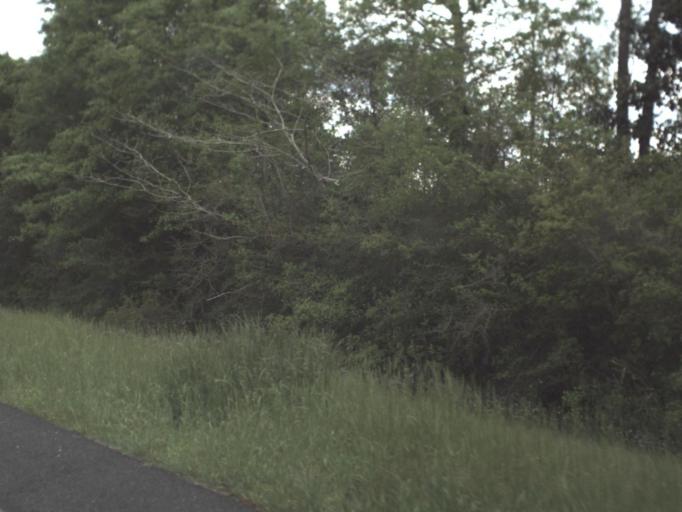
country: US
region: Florida
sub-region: Escambia County
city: Molino
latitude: 30.8009
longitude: -87.3357
